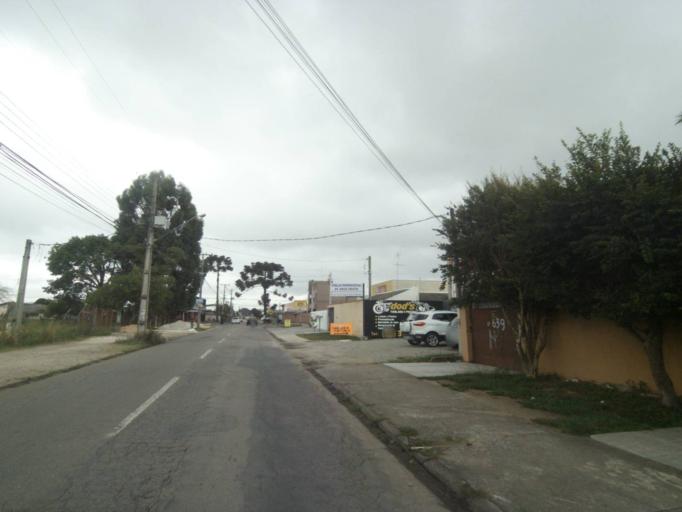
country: BR
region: Parana
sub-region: Pinhais
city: Pinhais
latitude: -25.4421
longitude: -49.1784
